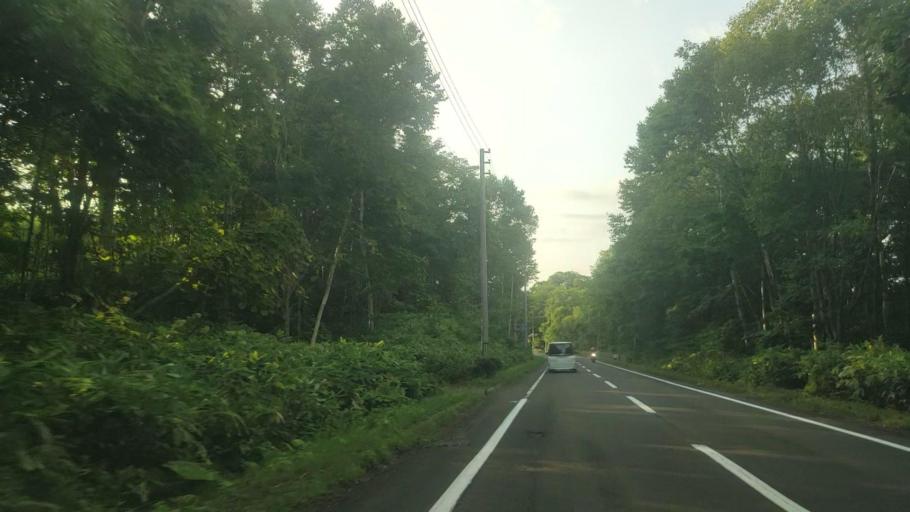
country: JP
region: Hokkaido
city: Bibai
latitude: 43.1726
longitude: 142.0711
